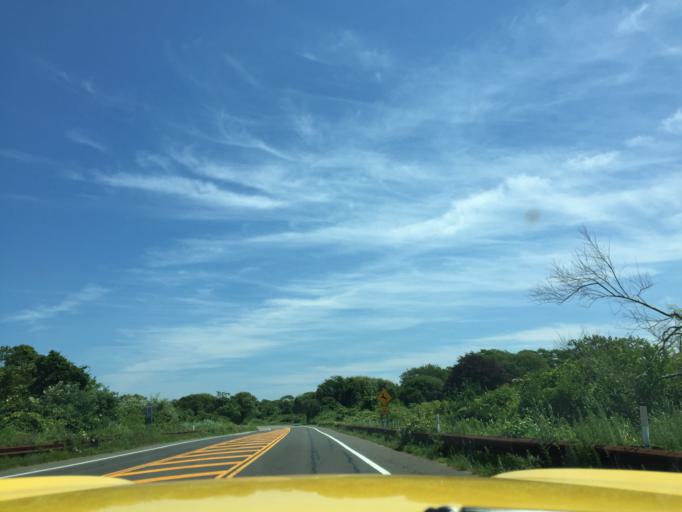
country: US
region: New York
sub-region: Suffolk County
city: Montauk
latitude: 41.0462
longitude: -71.9135
